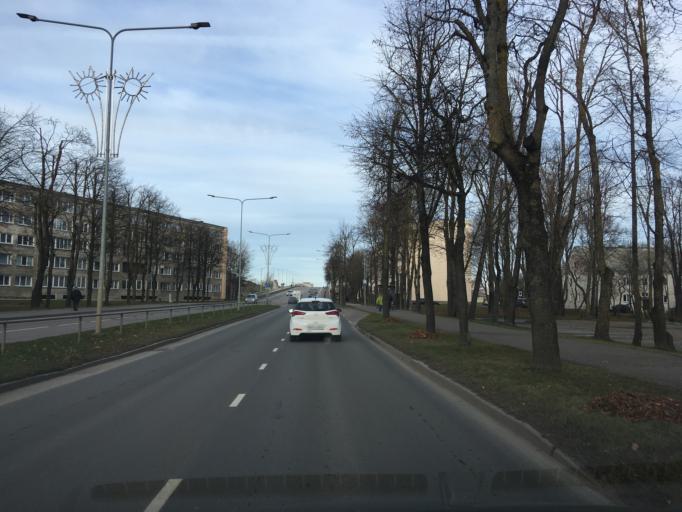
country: EE
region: Ida-Virumaa
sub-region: Narva linn
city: Narva
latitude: 59.3686
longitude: 28.1859
